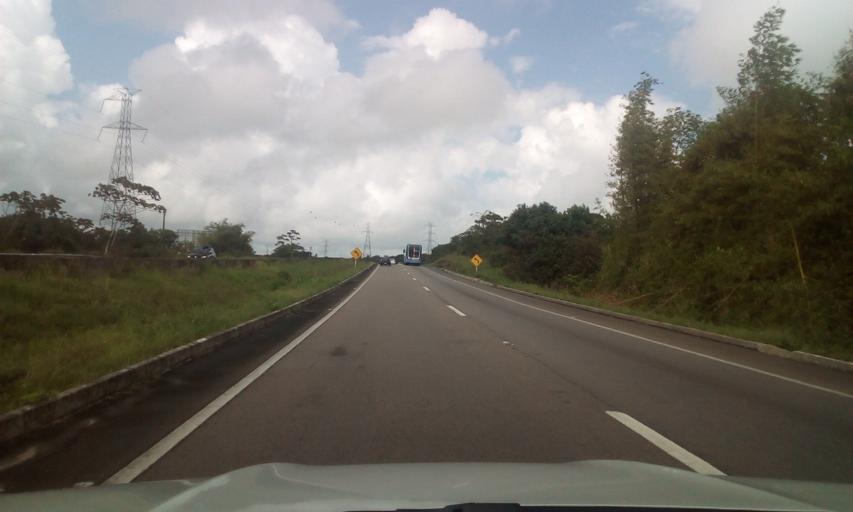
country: BR
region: Paraiba
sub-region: Conde
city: Conde
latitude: -7.3108
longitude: -34.9449
